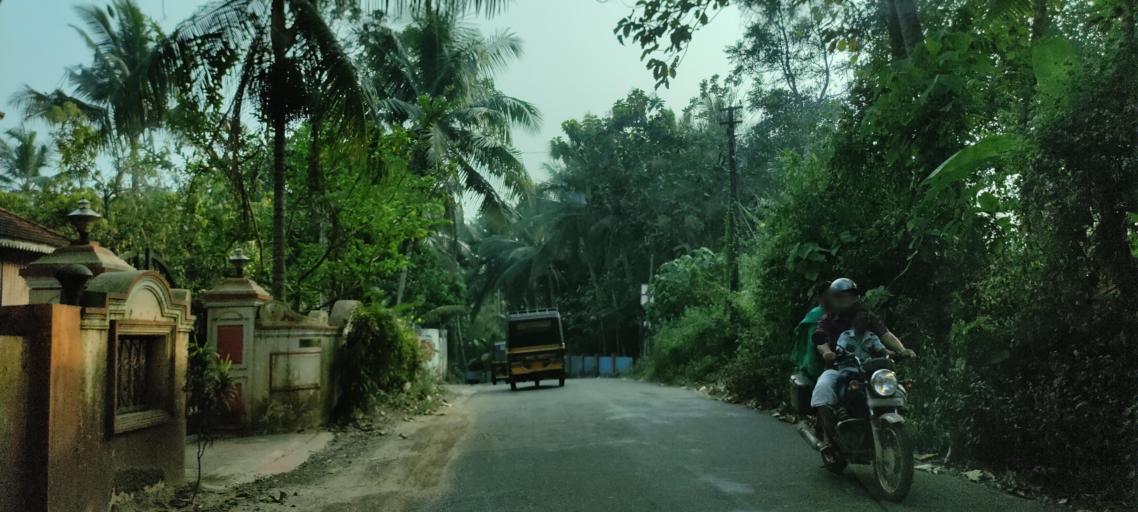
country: IN
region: Kerala
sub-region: Kottayam
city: Vaikam
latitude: 9.7540
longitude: 76.4920
